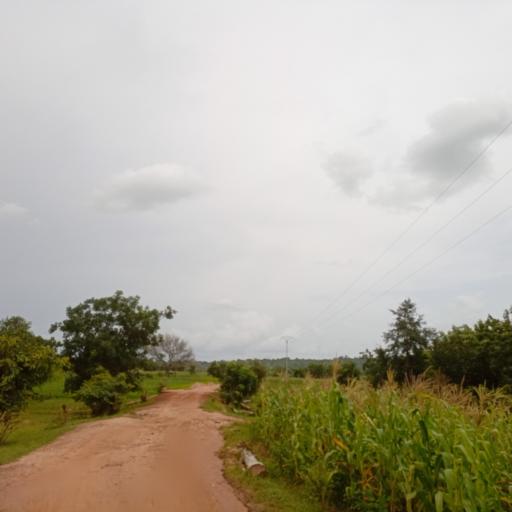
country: TG
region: Savanes
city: Dapaong
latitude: 10.8092
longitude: 0.0272
